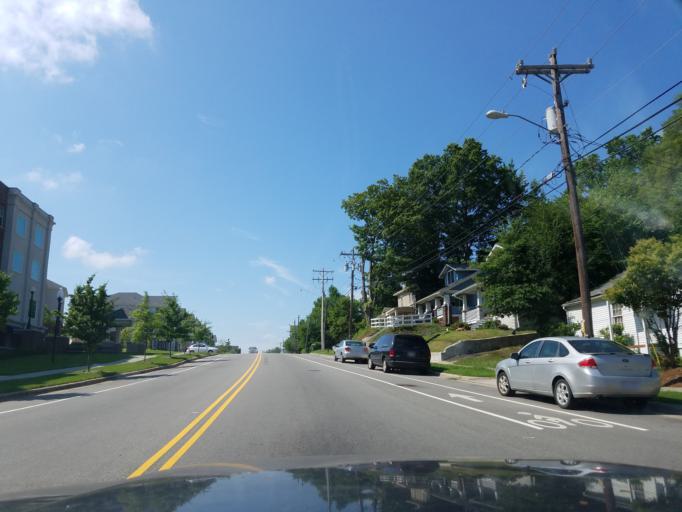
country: US
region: North Carolina
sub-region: Durham County
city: Durham
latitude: 35.9873
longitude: -78.9027
